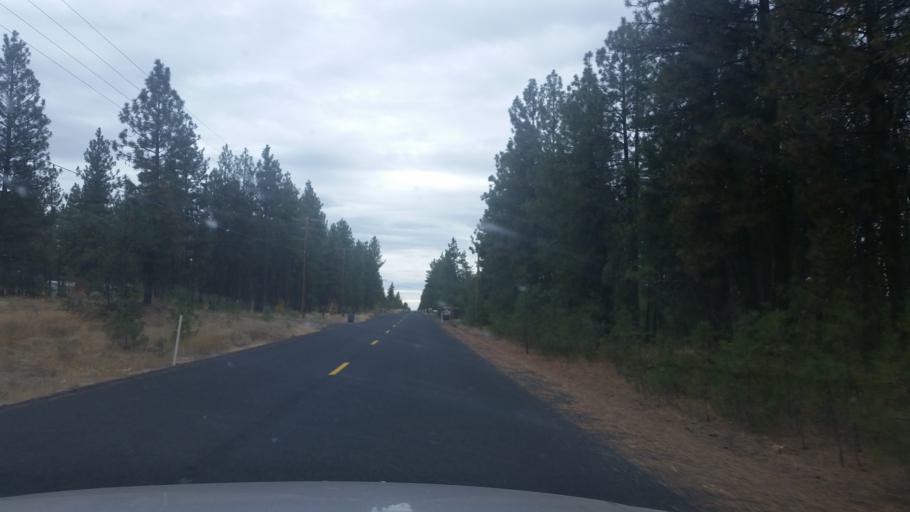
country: US
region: Washington
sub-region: Spokane County
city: Medical Lake
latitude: 47.4738
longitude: -117.7792
